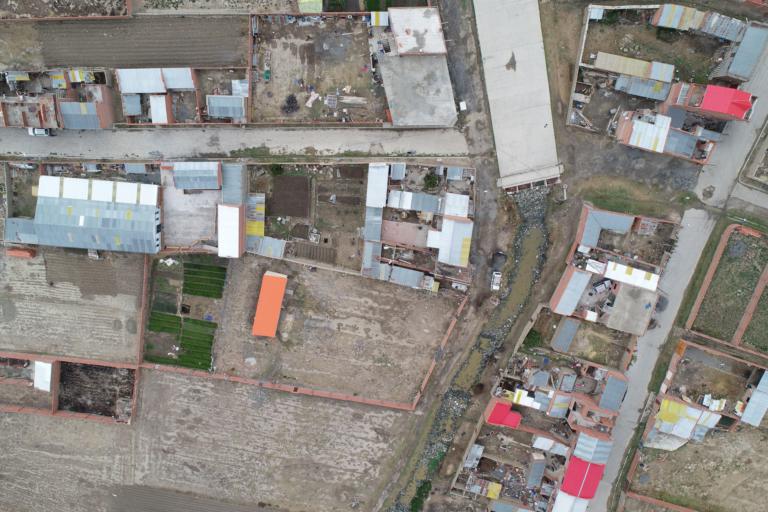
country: BO
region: La Paz
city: Achacachi
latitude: -16.0505
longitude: -68.6841
